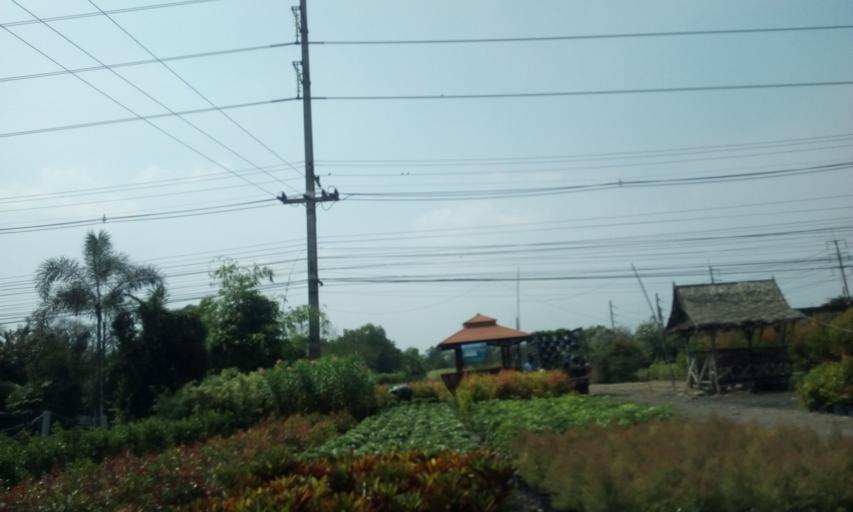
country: TH
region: Nakhon Nayok
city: Ongkharak
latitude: 14.1000
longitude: 100.9439
